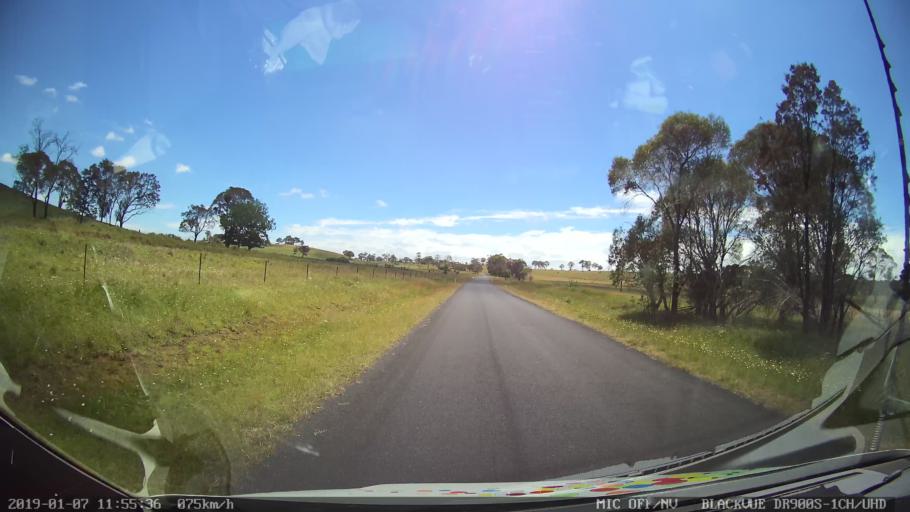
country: AU
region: New South Wales
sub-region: Guyra
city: Guyra
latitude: -30.2835
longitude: 151.6708
